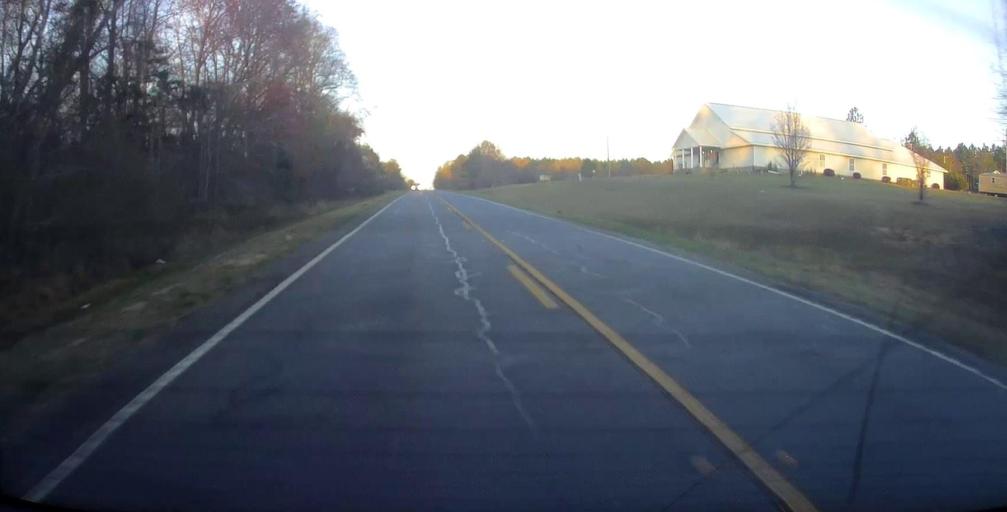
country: US
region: Georgia
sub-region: Dodge County
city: Eastman
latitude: 32.2756
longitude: -83.1146
